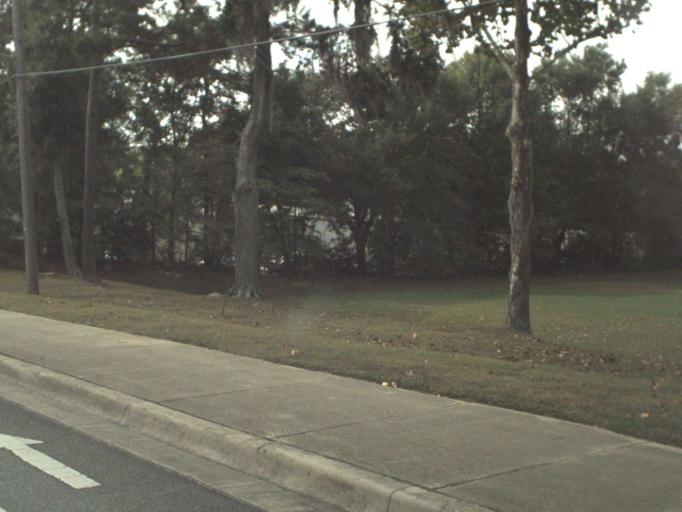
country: US
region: Florida
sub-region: Leon County
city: Tallahassee
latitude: 30.4396
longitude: -84.2267
